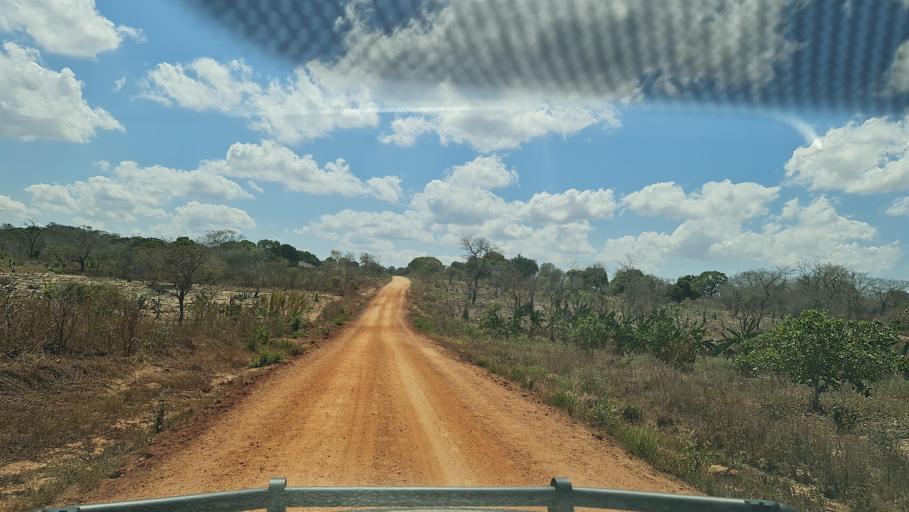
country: MZ
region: Nampula
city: Nacala
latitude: -14.1753
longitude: 40.2339
